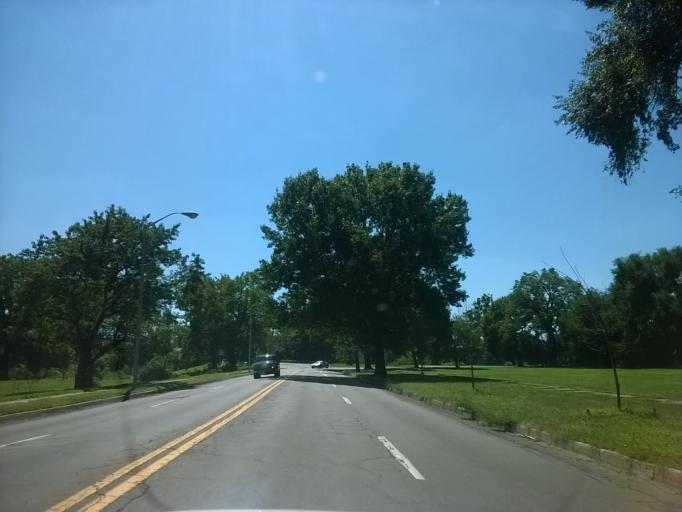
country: US
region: Indiana
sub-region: Marion County
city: Indianapolis
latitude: 39.7993
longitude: -86.1643
